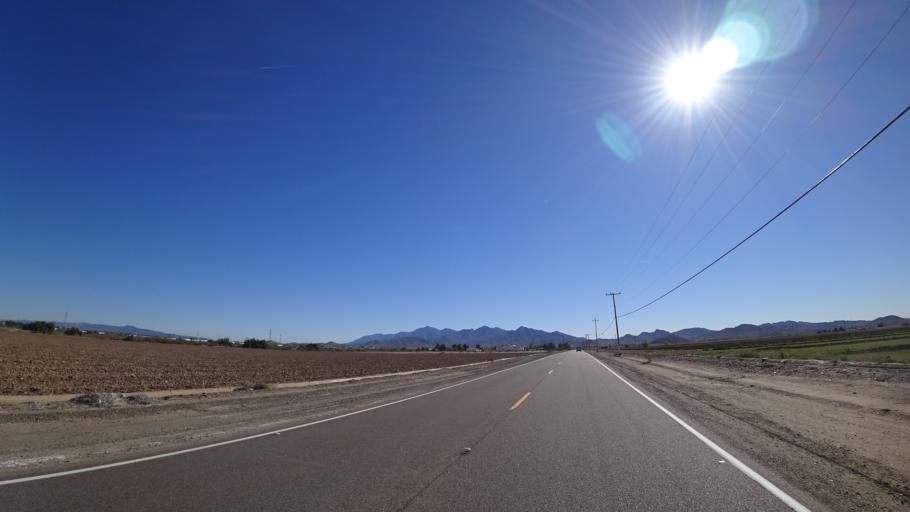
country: US
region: Arizona
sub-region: Maricopa County
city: Goodyear
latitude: 33.4163
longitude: -112.3578
